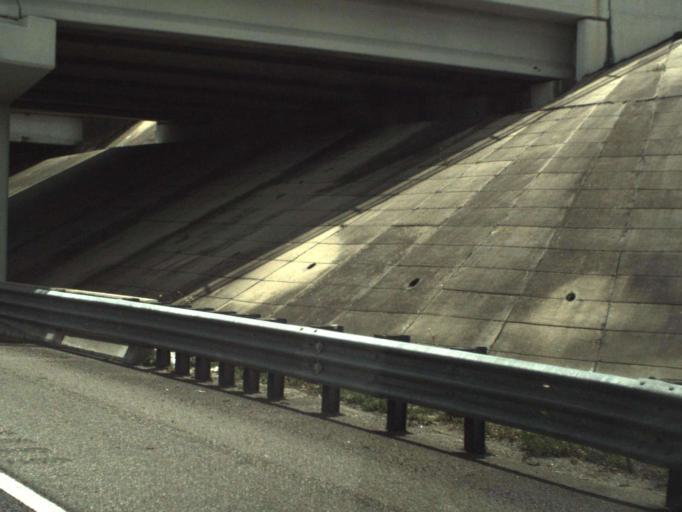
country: US
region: Florida
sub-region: Volusia County
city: Lake Helen
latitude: 28.9556
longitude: -81.2577
